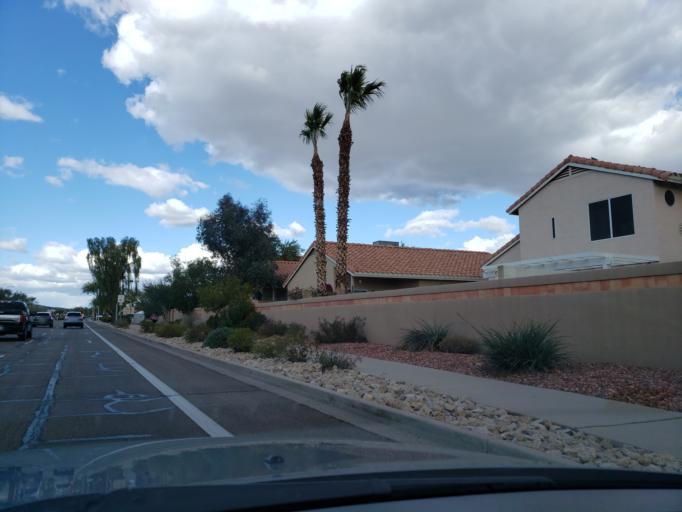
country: US
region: Arizona
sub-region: Maricopa County
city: Guadalupe
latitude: 33.3018
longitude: -111.9972
